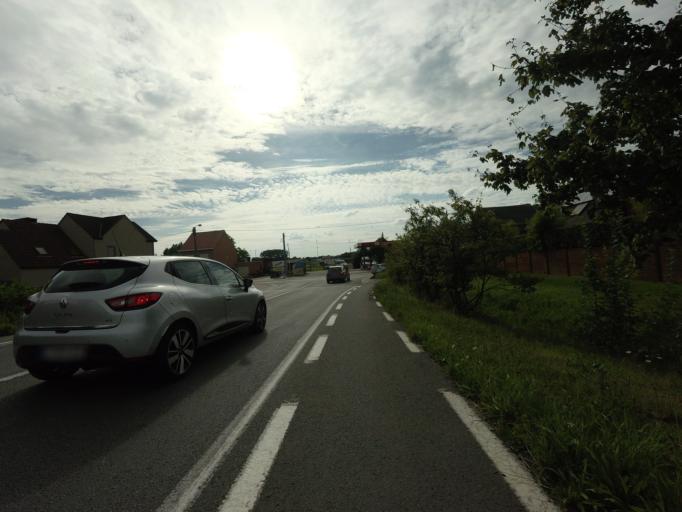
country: BE
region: Flanders
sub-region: Provincie Vlaams-Brabant
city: Londerzeel
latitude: 51.0180
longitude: 4.3160
